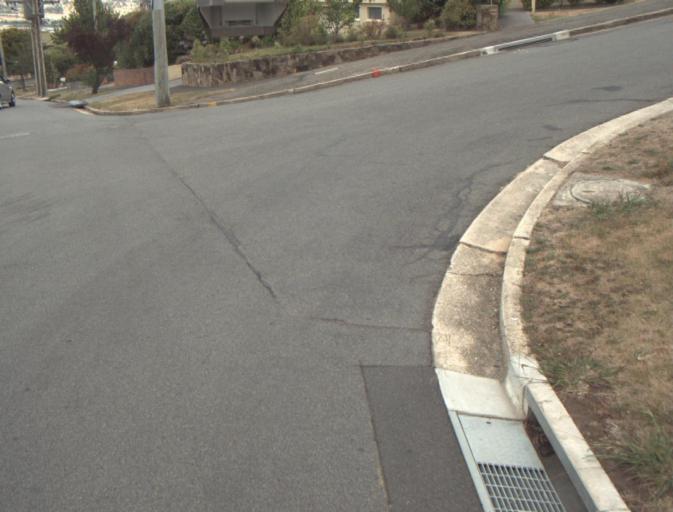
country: AU
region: Tasmania
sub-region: Launceston
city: Launceston
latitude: -41.4384
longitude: 147.1180
